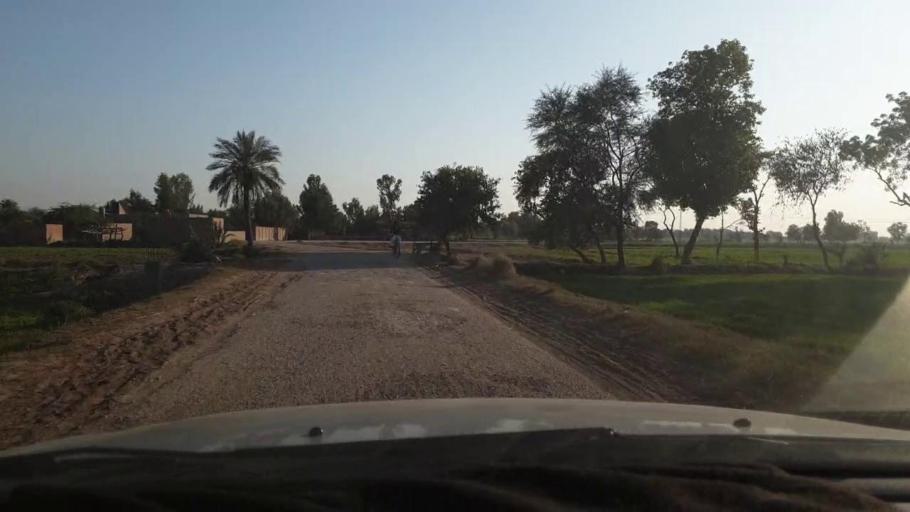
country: PK
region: Sindh
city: Mirpur Mathelo
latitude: 28.0114
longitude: 69.5405
